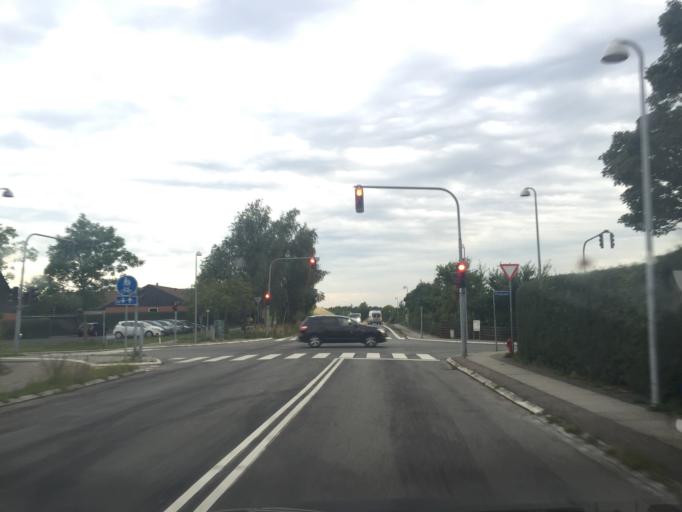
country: DK
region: Zealand
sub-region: Roskilde Kommune
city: Gundsomagle
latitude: 55.7389
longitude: 12.1486
